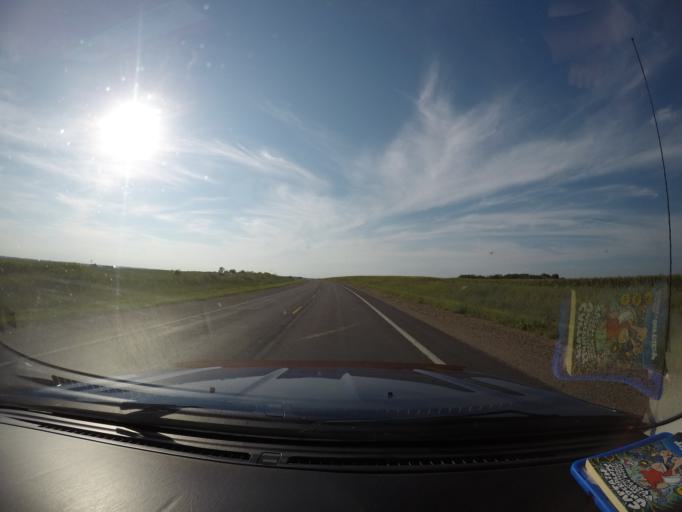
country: US
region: Kansas
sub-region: Atchison County
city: Atchison
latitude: 39.4288
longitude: -95.0756
